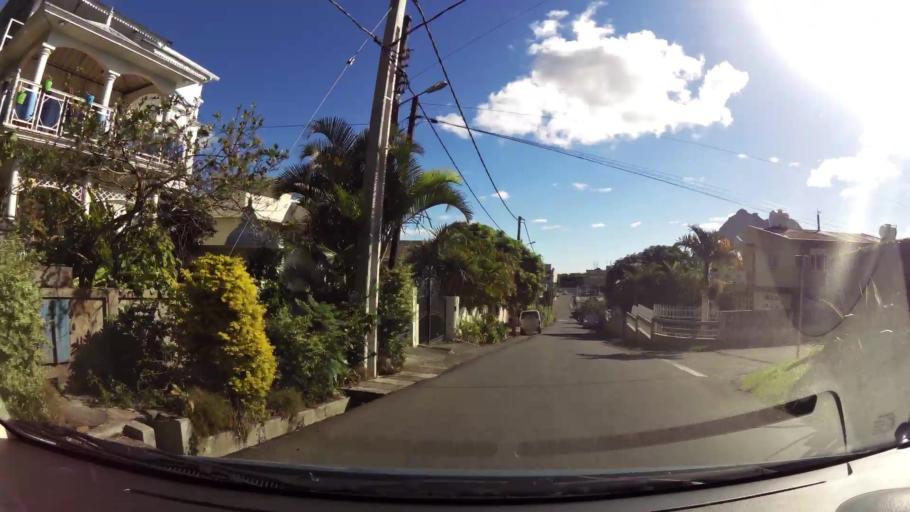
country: MU
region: Plaines Wilhems
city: Quatre Bornes
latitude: -20.2760
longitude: 57.4793
